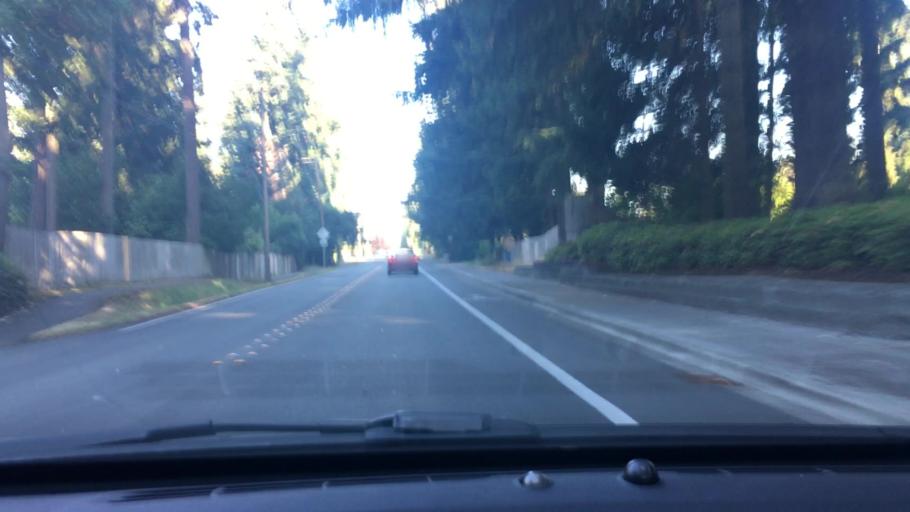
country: US
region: Washington
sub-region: King County
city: Sammamish
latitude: 47.6235
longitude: -122.1187
